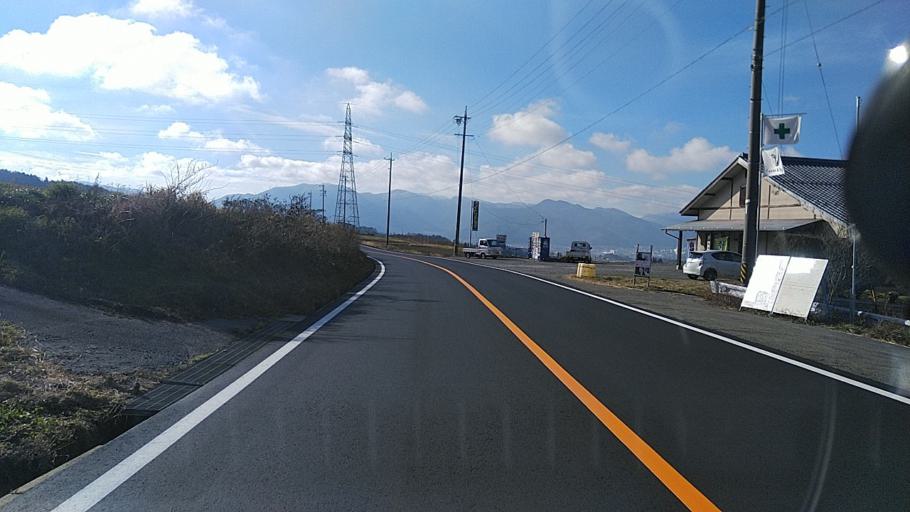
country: JP
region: Nagano
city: Shiojiri
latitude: 36.1418
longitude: 137.9894
